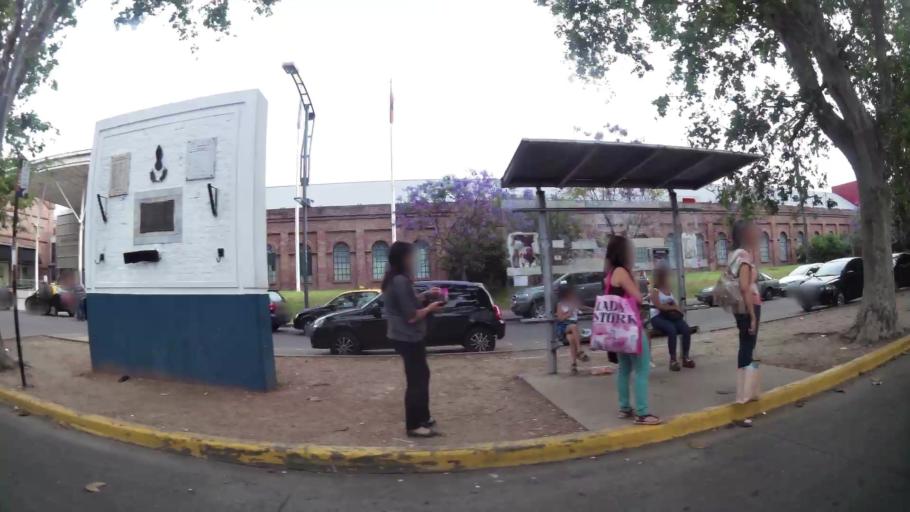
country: AR
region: Santa Fe
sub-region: Departamento de Rosario
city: Rosario
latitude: -32.9265
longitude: -60.6695
